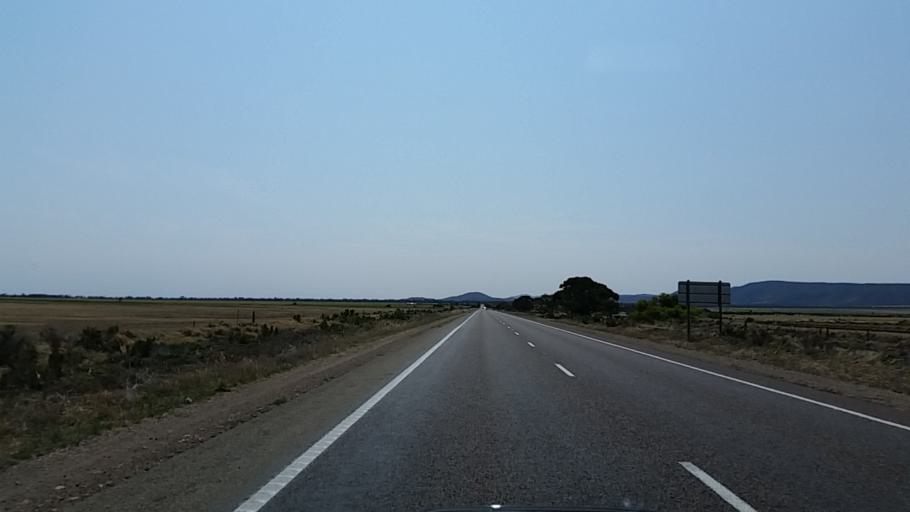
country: AU
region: South Australia
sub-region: Port Pirie City and Dists
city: Port Pirie
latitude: -32.8989
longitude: 137.9823
